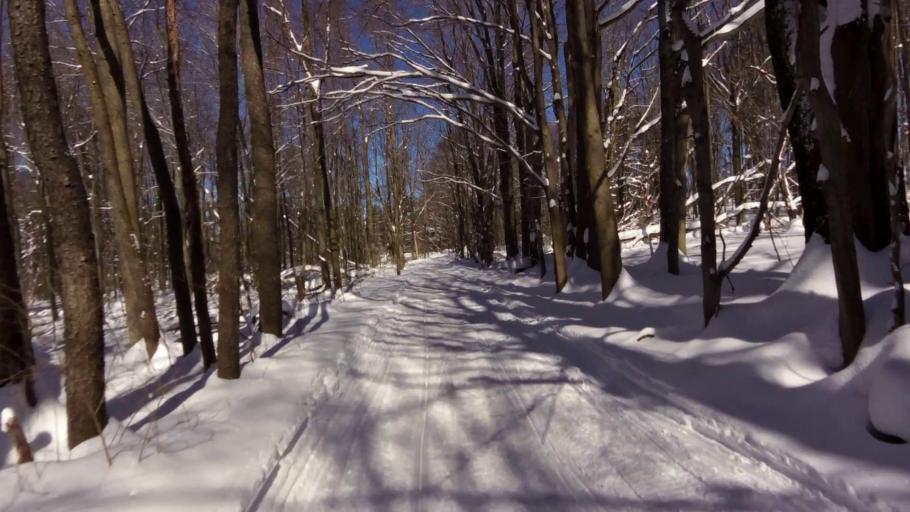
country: US
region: New York
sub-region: Chautauqua County
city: Mayville
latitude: 42.2353
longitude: -79.4204
